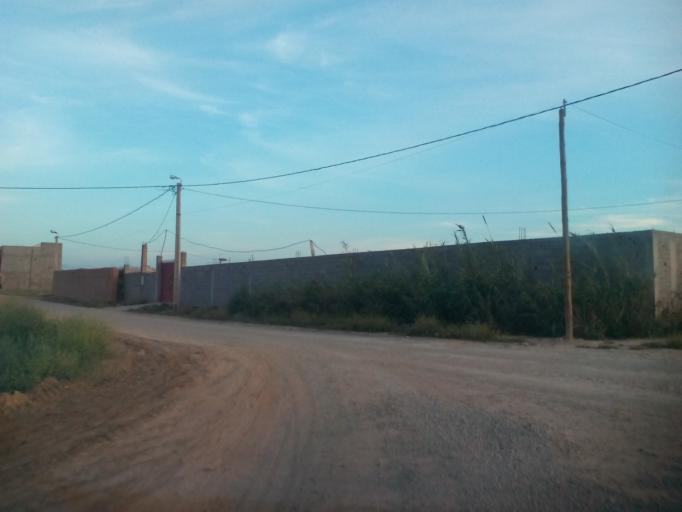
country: MA
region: Marrakech-Tensift-Al Haouz
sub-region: Marrakech
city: Marrakesh
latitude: 31.6281
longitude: -8.2879
